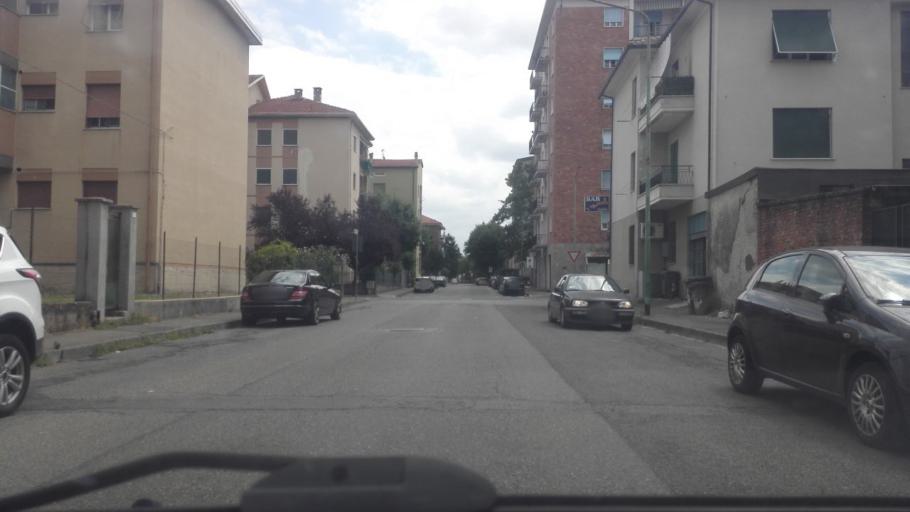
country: IT
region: Piedmont
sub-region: Provincia di Alessandria
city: Novi Ligure
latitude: 44.7688
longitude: 8.7902
